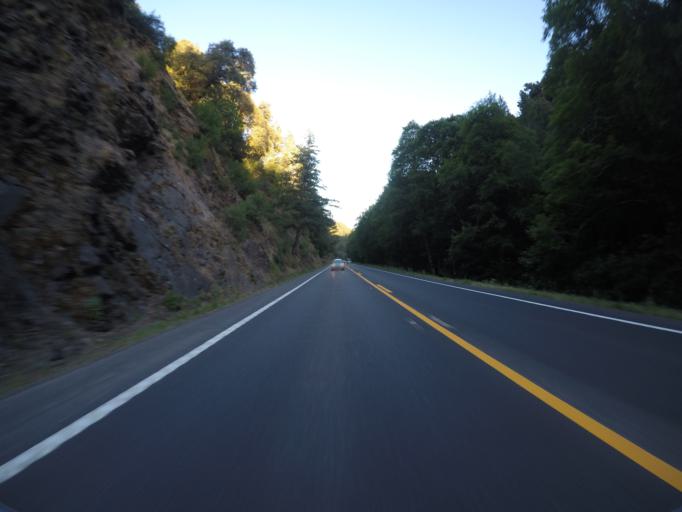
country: US
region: California
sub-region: Mendocino County
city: Laytonville
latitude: 39.8260
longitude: -123.5687
